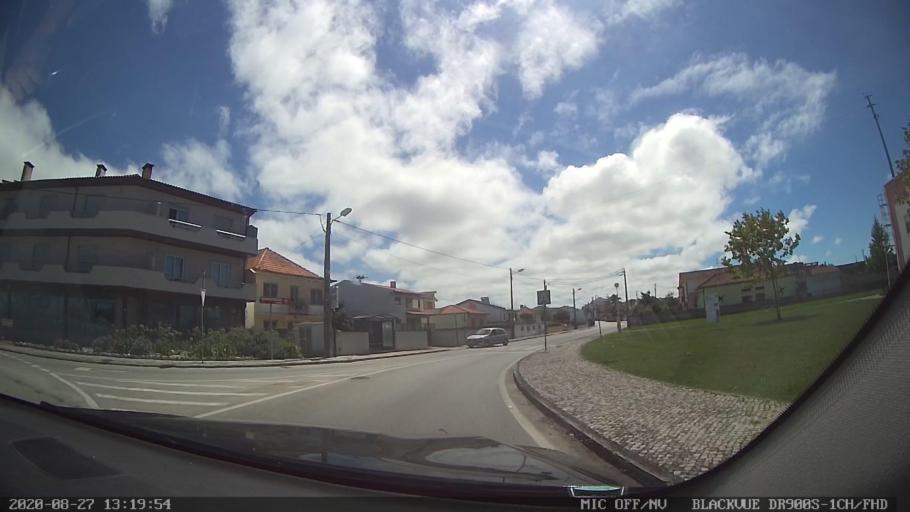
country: PT
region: Aveiro
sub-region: Vagos
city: Vagos
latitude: 40.5602
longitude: -8.6826
